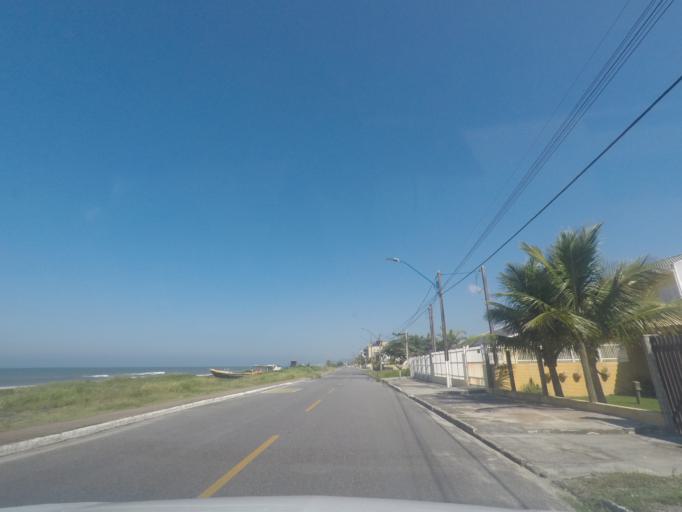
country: BR
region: Parana
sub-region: Pontal Do Parana
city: Pontal do Parana
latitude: -25.7592
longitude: -48.5056
